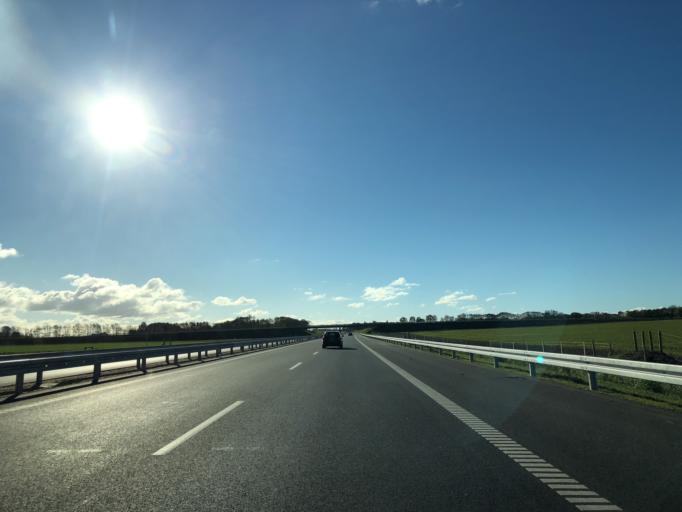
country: DK
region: Central Jutland
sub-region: Herning Kommune
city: Avlum
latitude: 56.3209
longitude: 8.7326
